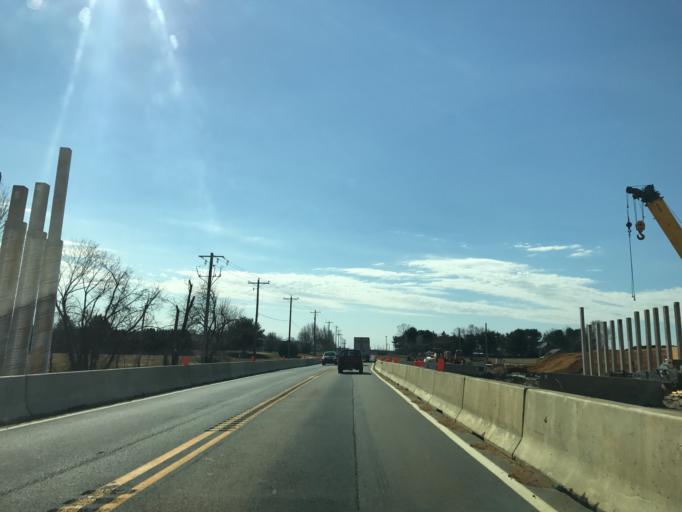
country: US
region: Delaware
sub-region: New Castle County
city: Middletown
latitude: 39.4889
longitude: -75.7171
